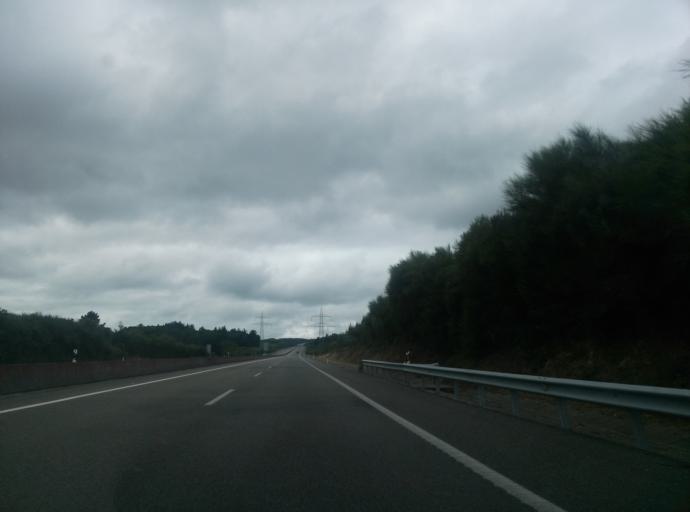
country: ES
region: Galicia
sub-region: Provincia de Lugo
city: Vilalba
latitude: 43.3280
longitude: -7.6965
